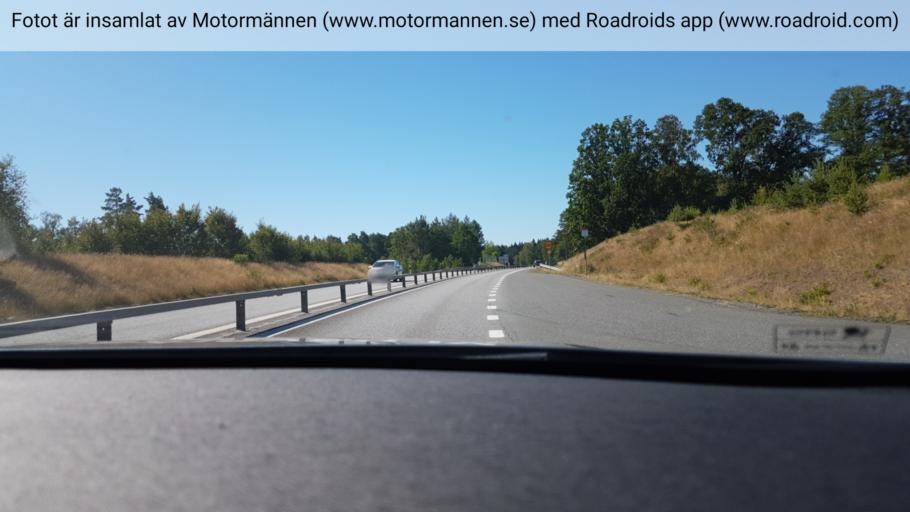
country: SE
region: Joenkoeping
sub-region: Jonkopings Kommun
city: Bankeryd
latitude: 57.8772
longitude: 14.1043
